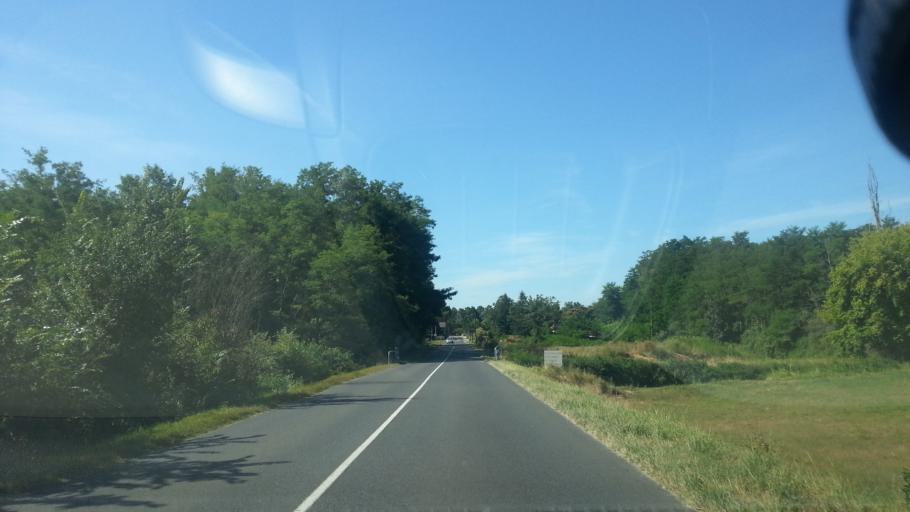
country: FR
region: Aquitaine
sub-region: Departement de la Gironde
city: Illats
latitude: 44.6236
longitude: -0.3703
